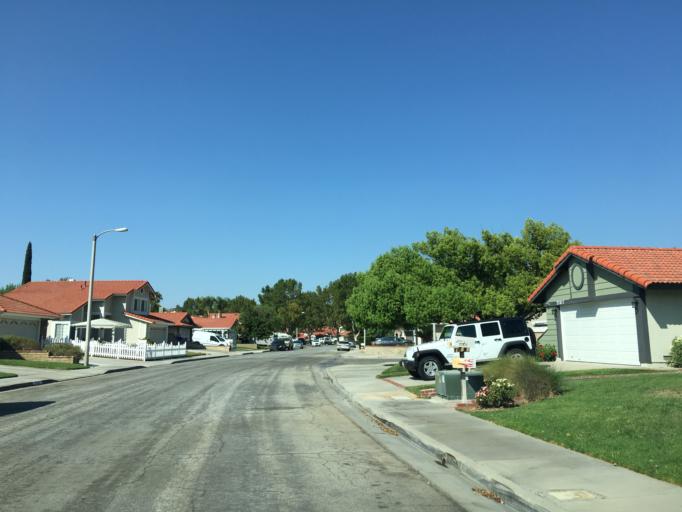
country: US
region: California
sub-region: Los Angeles County
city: Valencia
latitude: 34.4541
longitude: -118.6209
